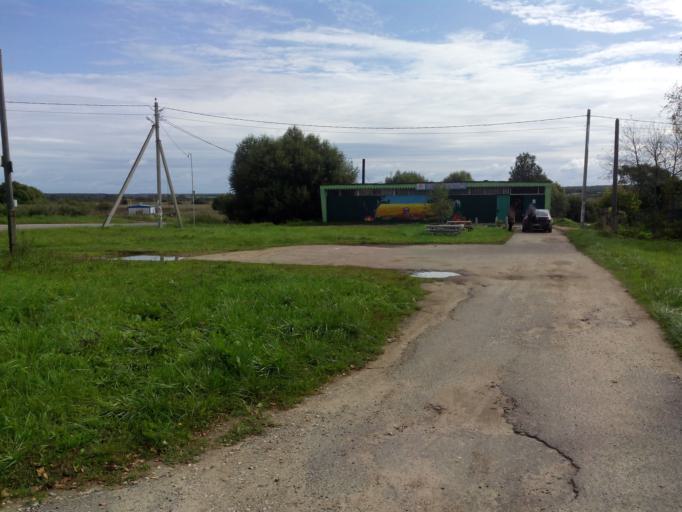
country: RU
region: Moskovskaya
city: Severnyy
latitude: 56.6468
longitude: 37.7302
